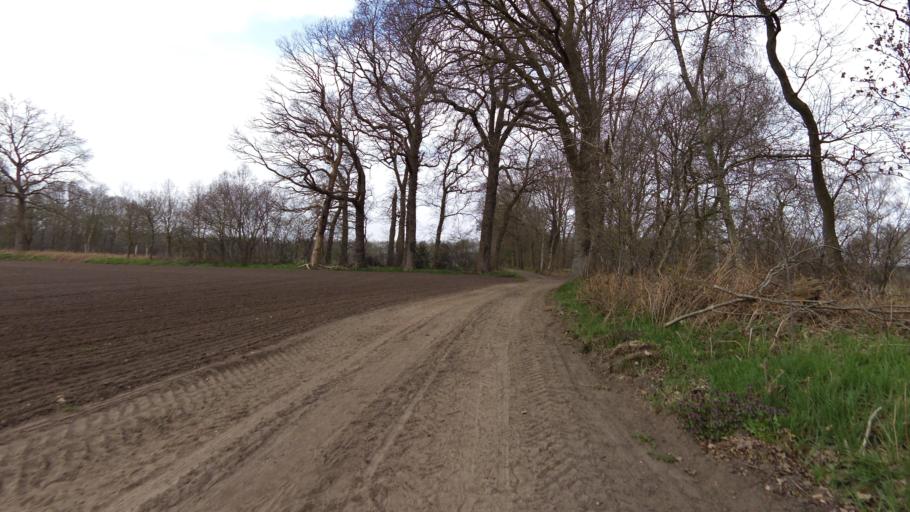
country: NL
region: Gelderland
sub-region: Gemeente Nijkerk
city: Nijkerk
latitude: 52.2253
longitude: 5.5495
